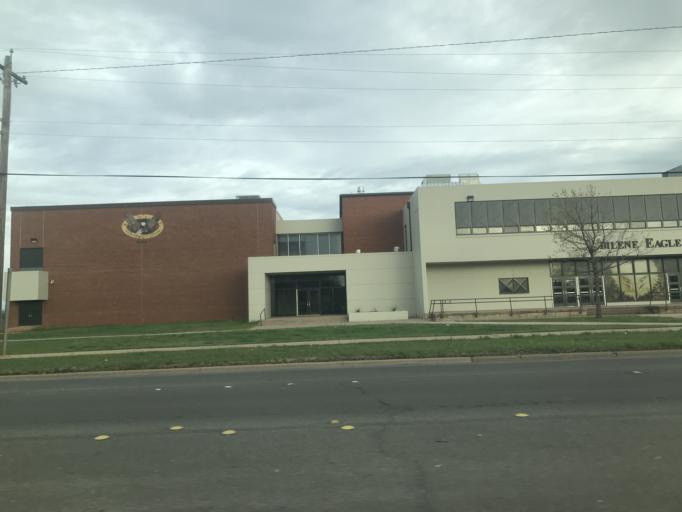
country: US
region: Texas
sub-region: Taylor County
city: Abilene
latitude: 32.4570
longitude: -99.7578
